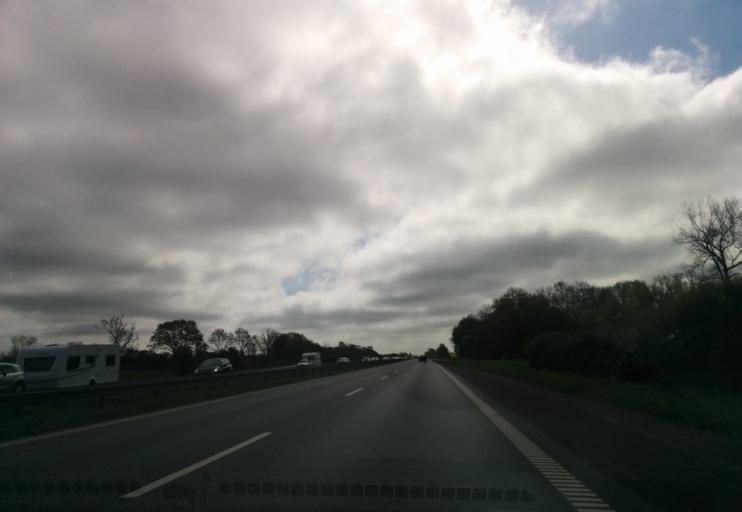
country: DK
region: South Denmark
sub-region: Assens Kommune
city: Arup
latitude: 55.4261
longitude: 10.0020
